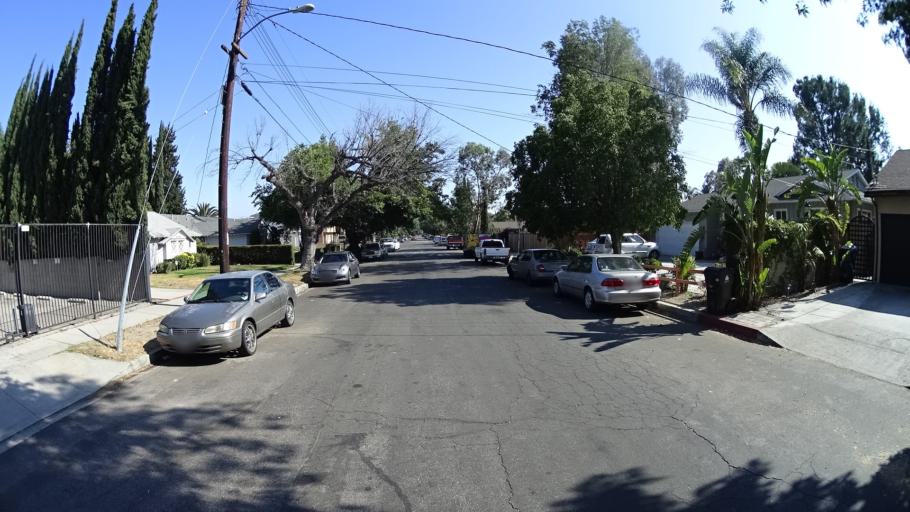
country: US
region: California
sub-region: Los Angeles County
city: Van Nuys
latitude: 34.1933
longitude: -118.4269
